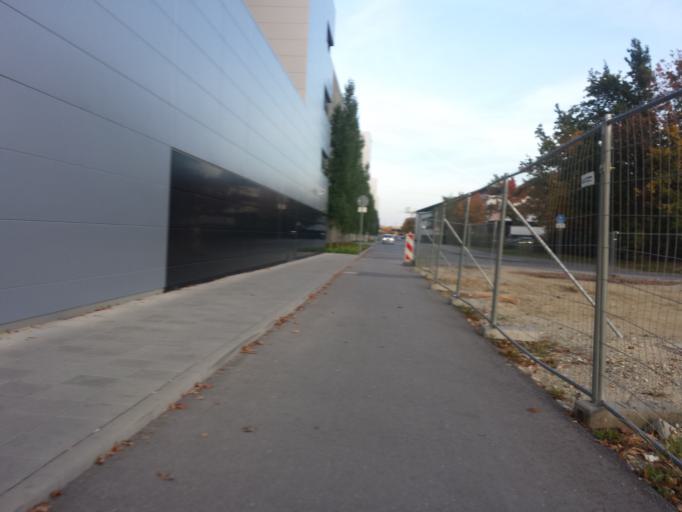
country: DE
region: Bavaria
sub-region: Upper Bavaria
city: Ingolstadt
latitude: 48.7814
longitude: 11.4185
